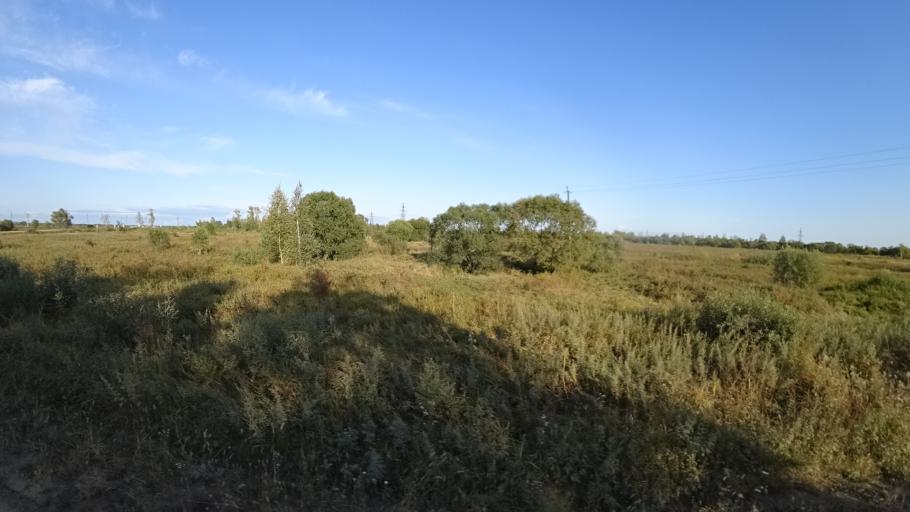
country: RU
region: Amur
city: Arkhara
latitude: 49.3684
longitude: 130.1360
